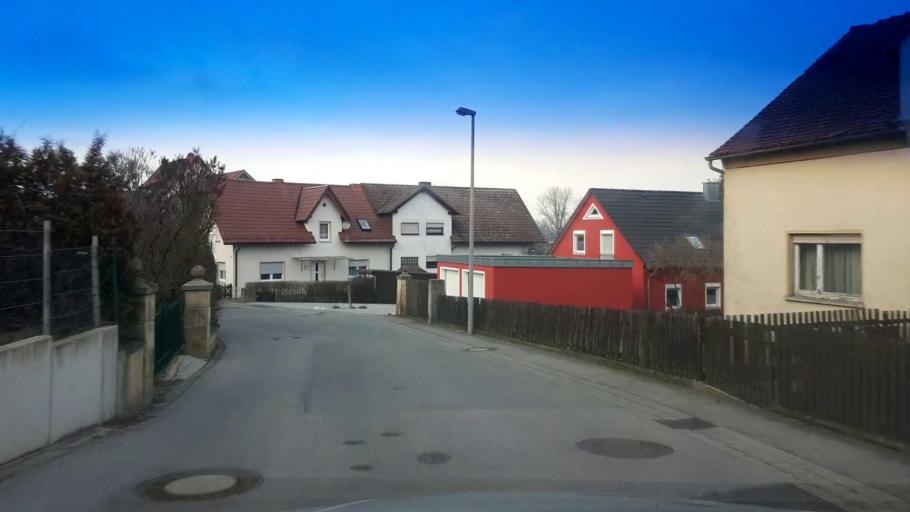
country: DE
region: Bavaria
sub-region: Upper Franconia
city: Hirschaid
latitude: 49.8033
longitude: 10.9881
